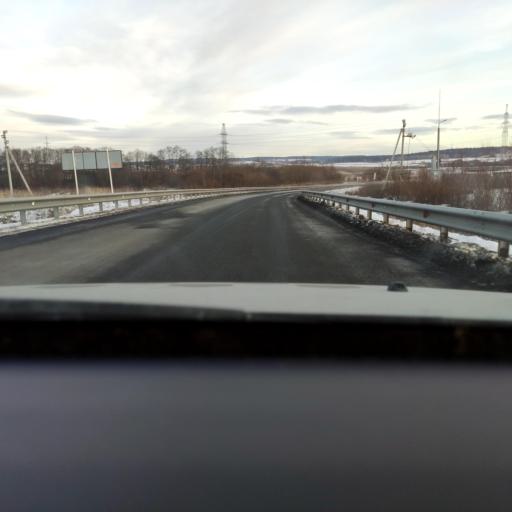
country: RU
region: Perm
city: Ferma
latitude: 57.9317
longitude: 56.3291
